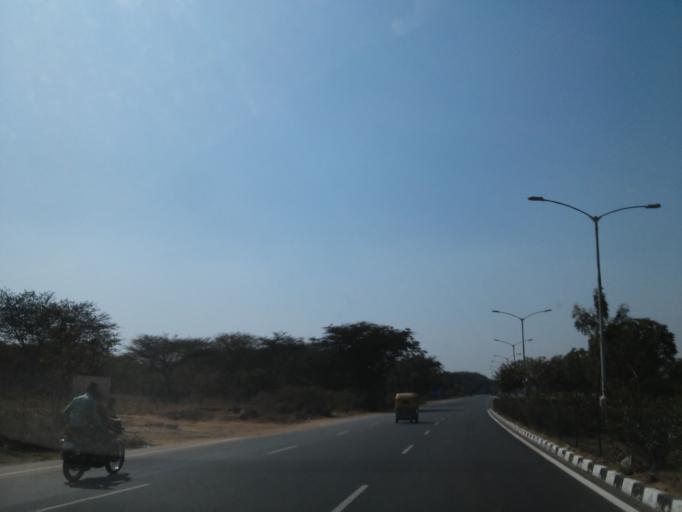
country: IN
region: Gujarat
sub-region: Gandhinagar
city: Ghandinagar
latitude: 23.2012
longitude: 72.6553
